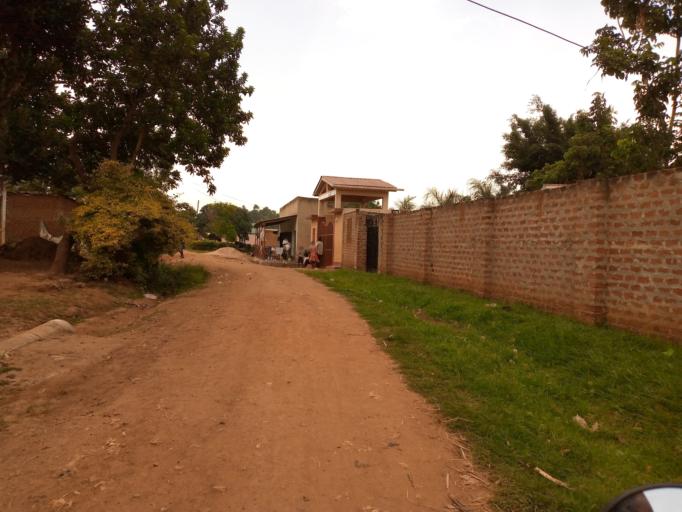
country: UG
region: Eastern Region
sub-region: Mbale District
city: Mbale
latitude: 1.0888
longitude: 34.1660
